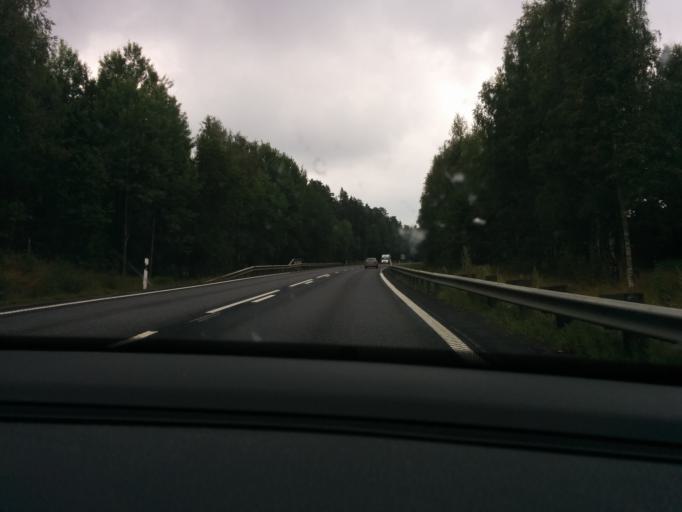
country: SE
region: Kronoberg
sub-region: Vaxjo Kommun
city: Vaexjoe
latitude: 56.8955
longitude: 14.8290
